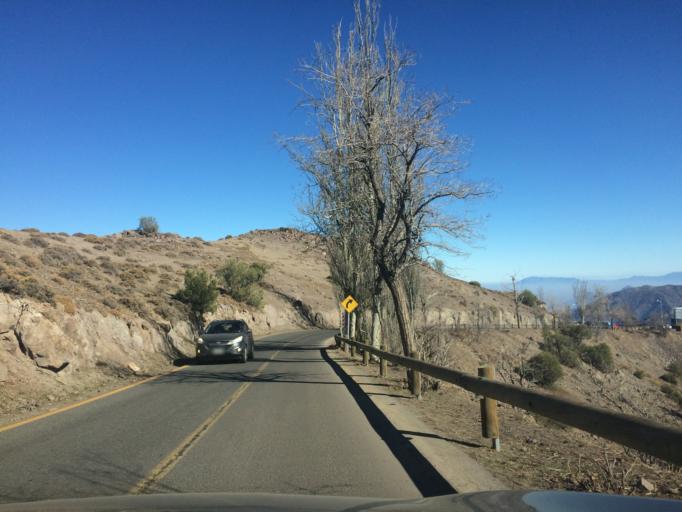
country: CL
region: Santiago Metropolitan
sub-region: Provincia de Santiago
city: Villa Presidente Frei, Nunoa, Santiago, Chile
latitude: -33.3567
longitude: -70.3217
